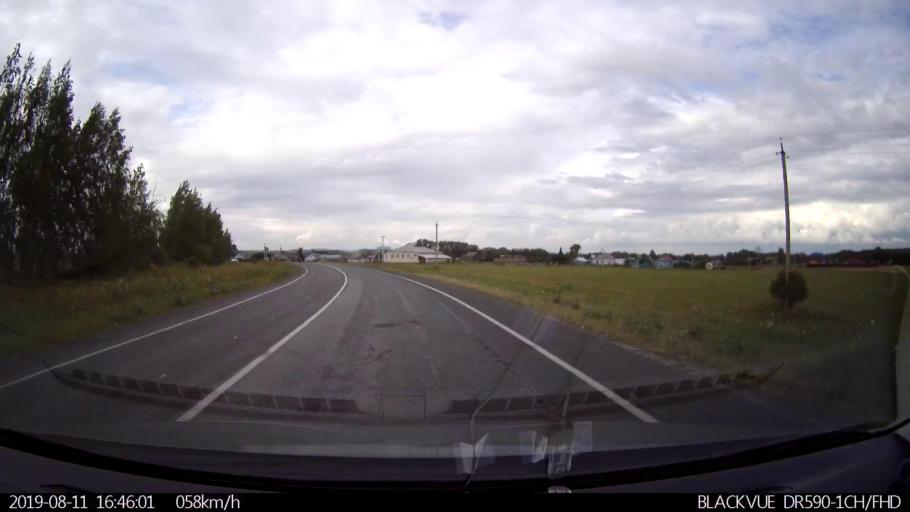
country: RU
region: Ulyanovsk
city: Mayna
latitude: 54.1950
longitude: 47.6886
